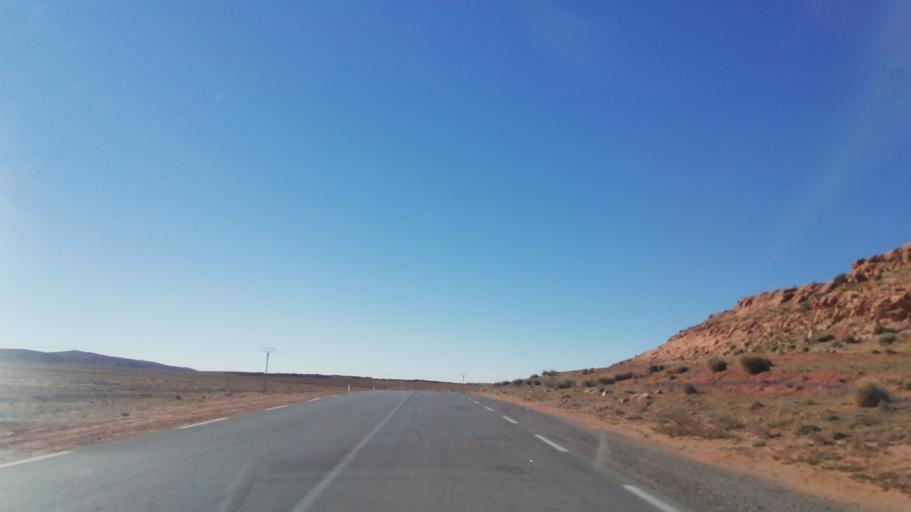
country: DZ
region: El Bayadh
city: El Bayadh
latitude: 33.6529
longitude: 1.4100
